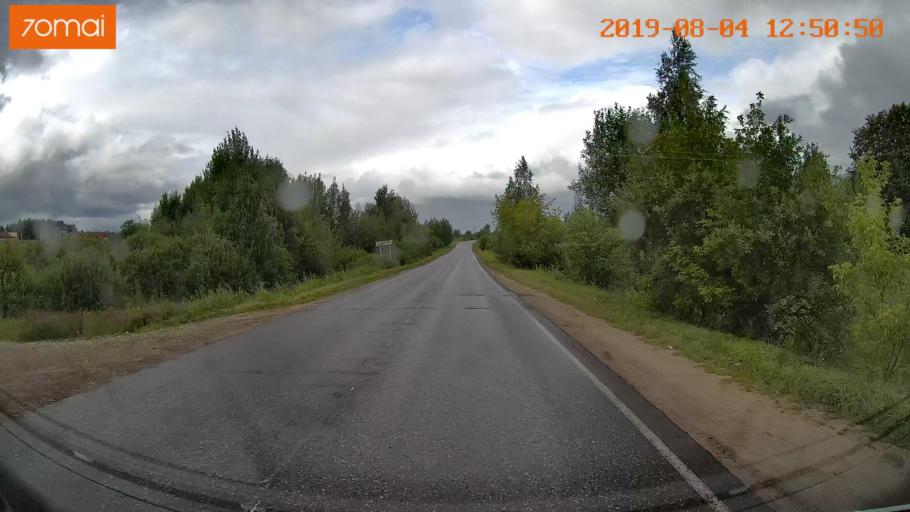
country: RU
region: Ivanovo
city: Novo-Talitsy
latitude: 57.0358
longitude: 40.8966
